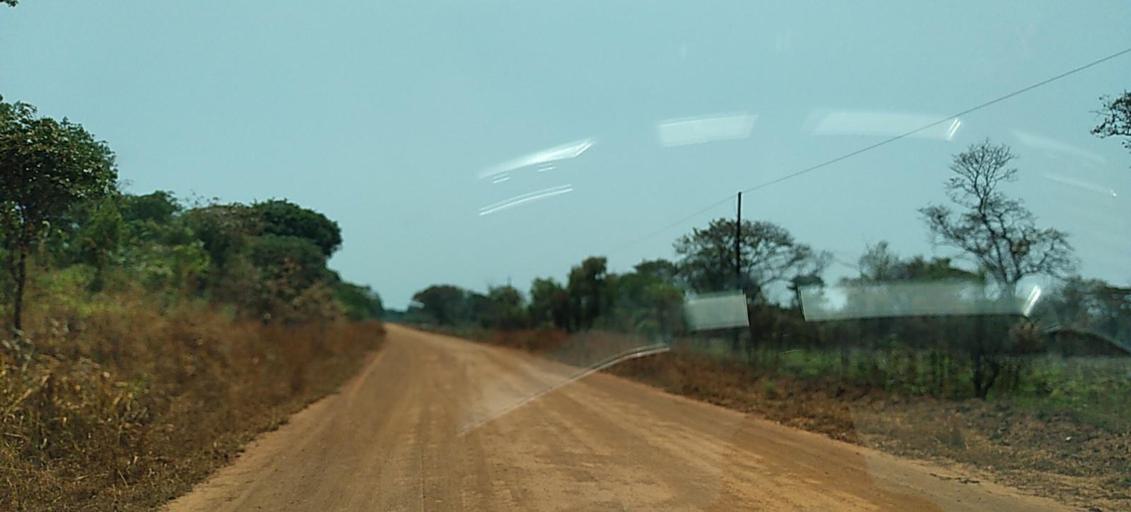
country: CD
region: Katanga
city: Kipushi
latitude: -11.9859
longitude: 26.8789
